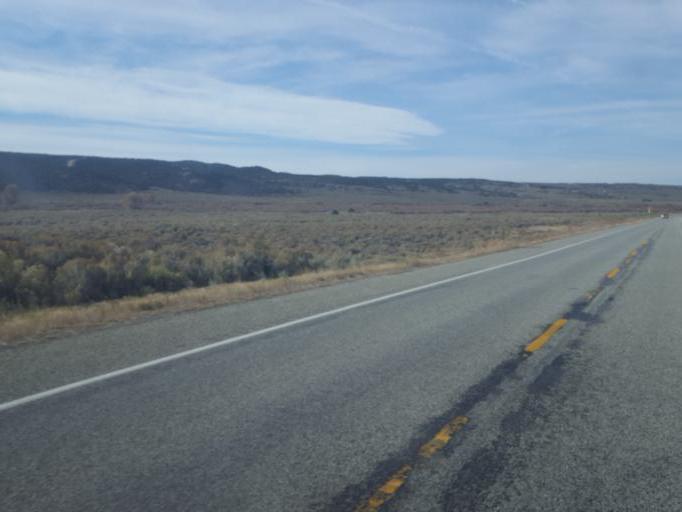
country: US
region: Colorado
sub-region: Costilla County
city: San Luis
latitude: 37.4340
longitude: -105.3928
